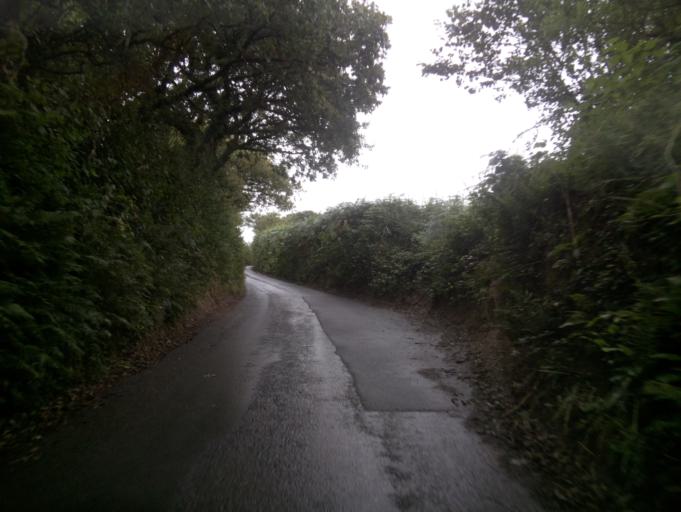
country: GB
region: England
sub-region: Devon
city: Kingsbridge
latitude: 50.3253
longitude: -3.7158
